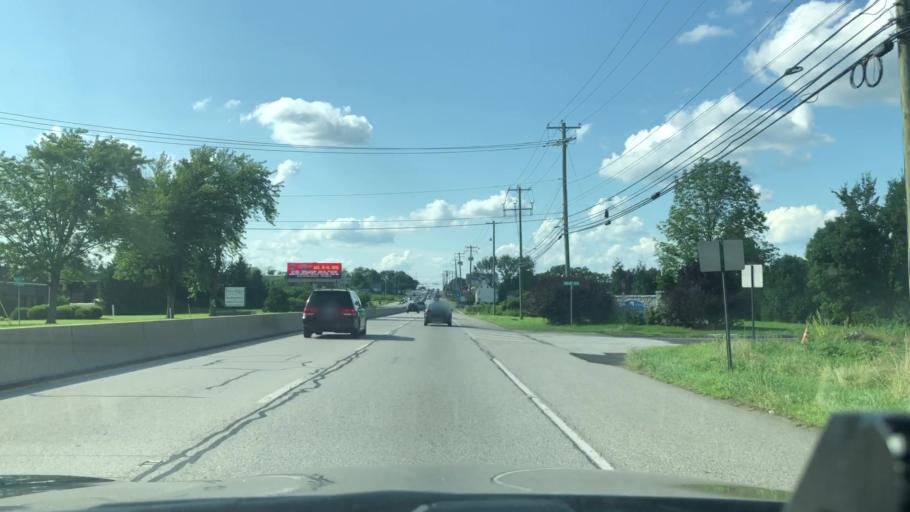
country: US
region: Pennsylvania
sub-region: Montgomery County
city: Spring House
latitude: 40.2125
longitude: -75.2259
